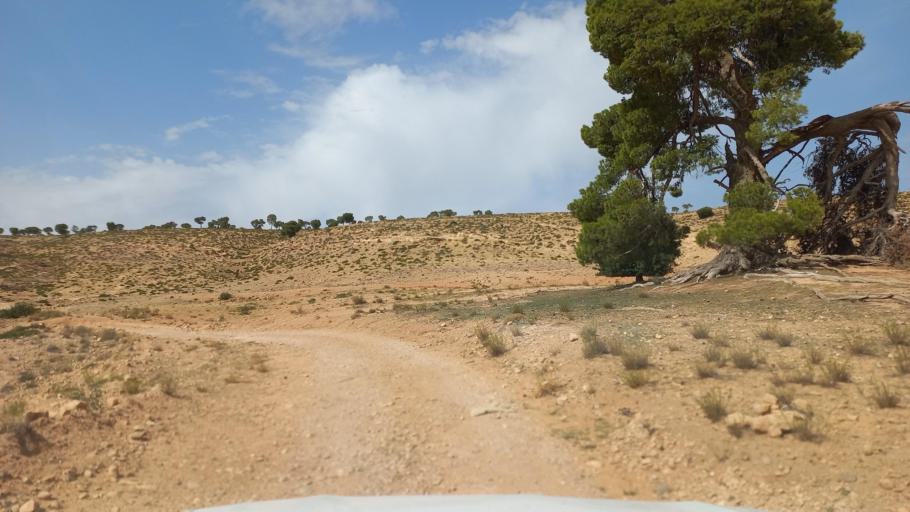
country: TN
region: Al Qasrayn
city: Kasserine
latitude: 35.3724
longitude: 8.8789
